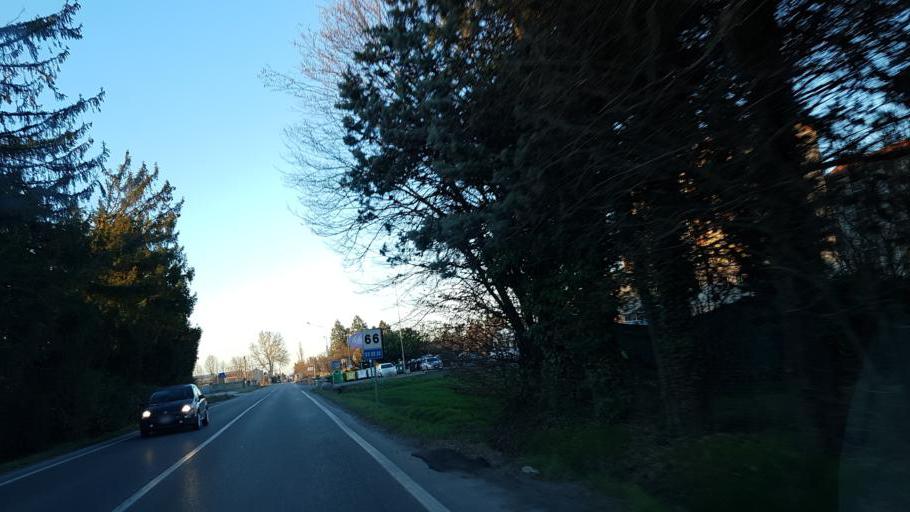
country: IT
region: Piedmont
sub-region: Provincia di Alessandria
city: Carbonara Scrivia
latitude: 44.8601
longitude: 8.8552
